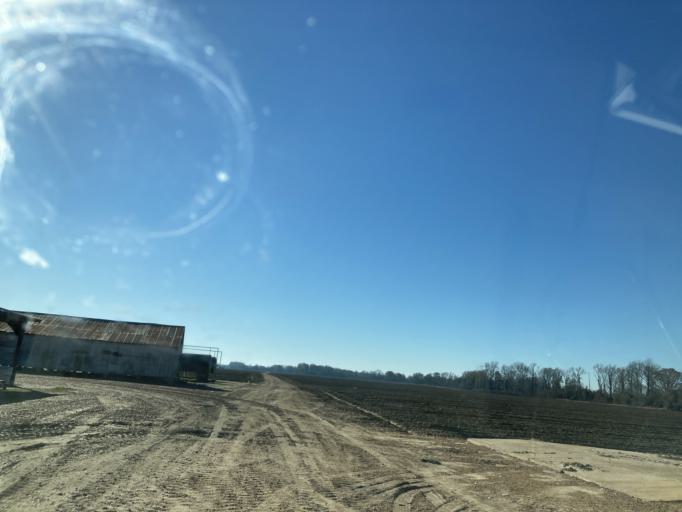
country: US
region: Mississippi
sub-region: Sharkey County
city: Rolling Fork
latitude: 32.8668
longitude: -90.6927
